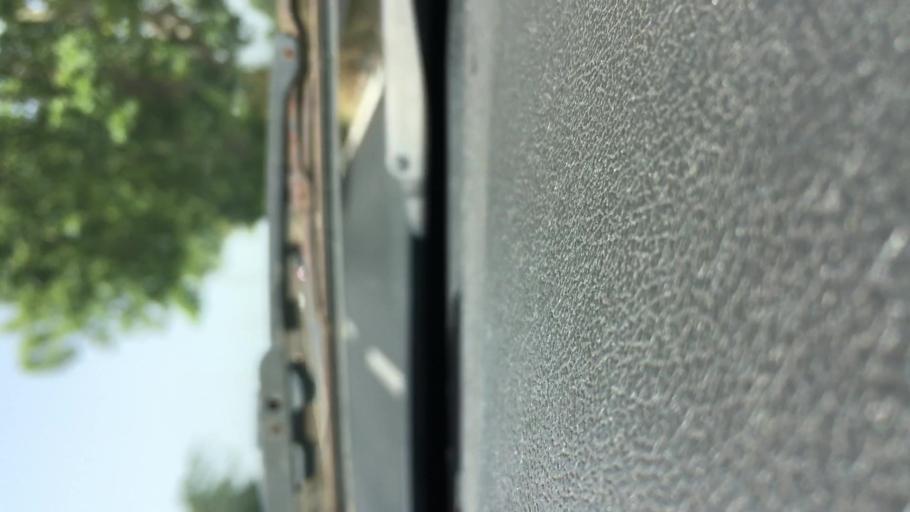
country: IT
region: Latium
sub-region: Citta metropolitana di Roma Capitale
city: Ciampino
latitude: 41.8332
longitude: 12.6104
